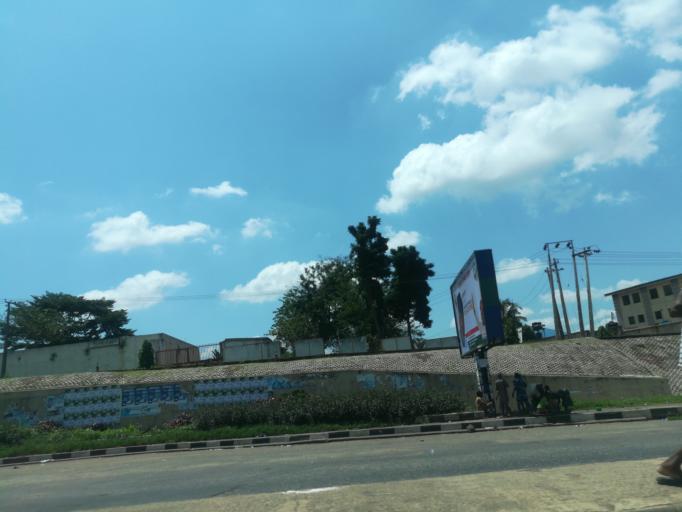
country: NG
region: Oyo
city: Ibadan
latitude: 7.3636
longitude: 3.8645
